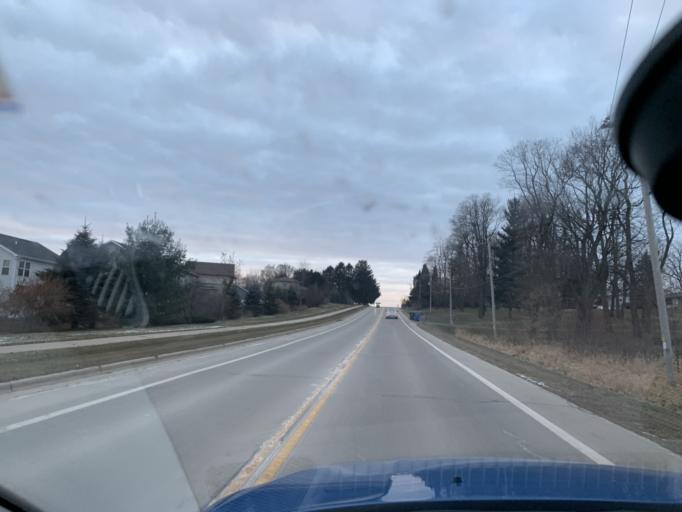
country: US
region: Wisconsin
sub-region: Dane County
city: Verona
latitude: 43.0457
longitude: -89.5391
